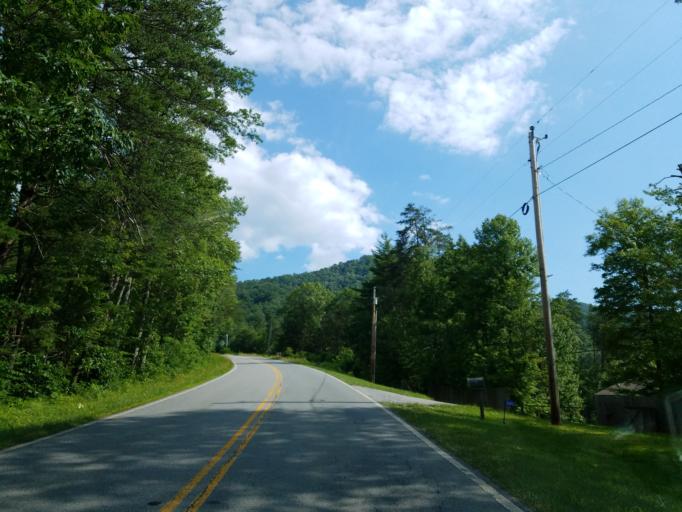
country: US
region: Georgia
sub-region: Fannin County
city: Blue Ridge
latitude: 34.8250
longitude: -84.3055
